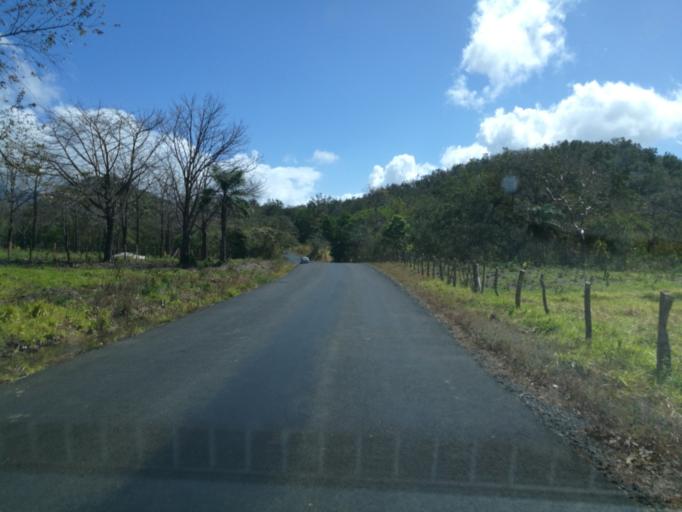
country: CR
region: Guanacaste
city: Liberia
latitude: 10.7461
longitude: -85.3783
